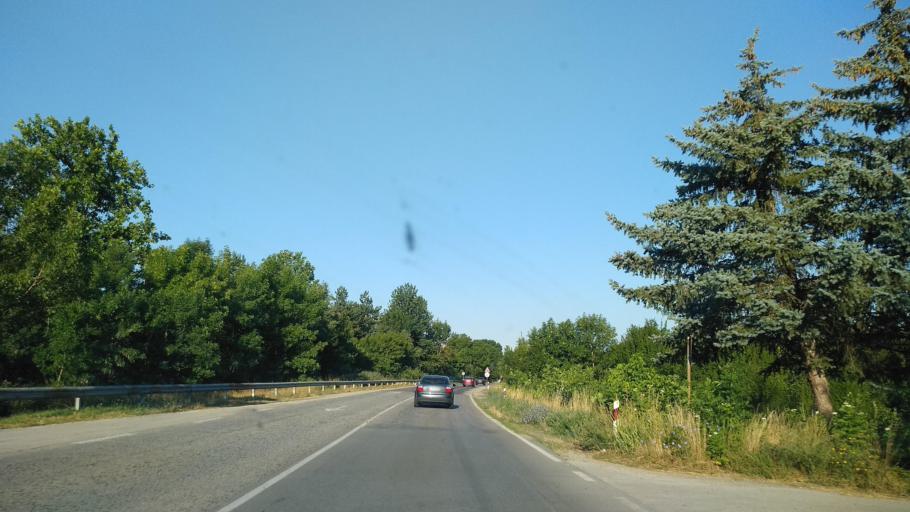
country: BG
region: Veliko Turnovo
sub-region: Obshtina Pavlikeni
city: Byala Cherkva
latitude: 43.0847
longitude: 25.3642
